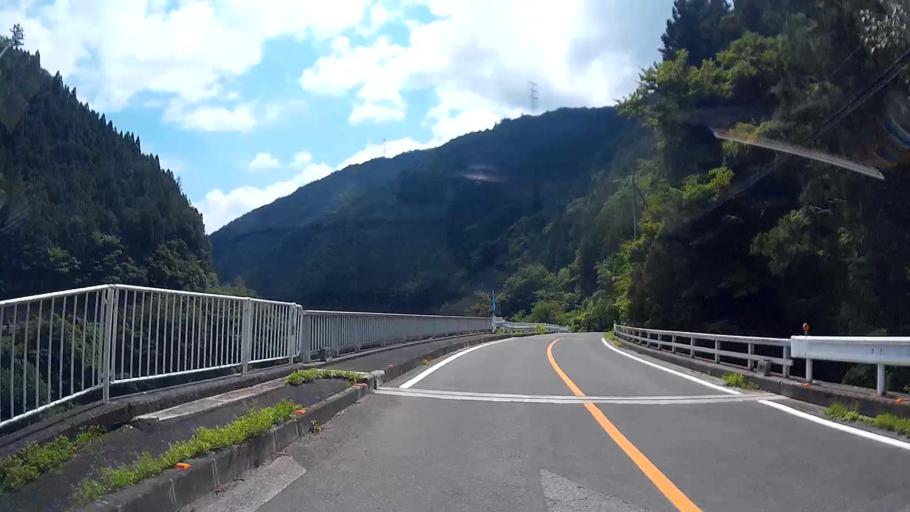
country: JP
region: Saitama
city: Chichibu
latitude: 35.9242
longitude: 139.0672
